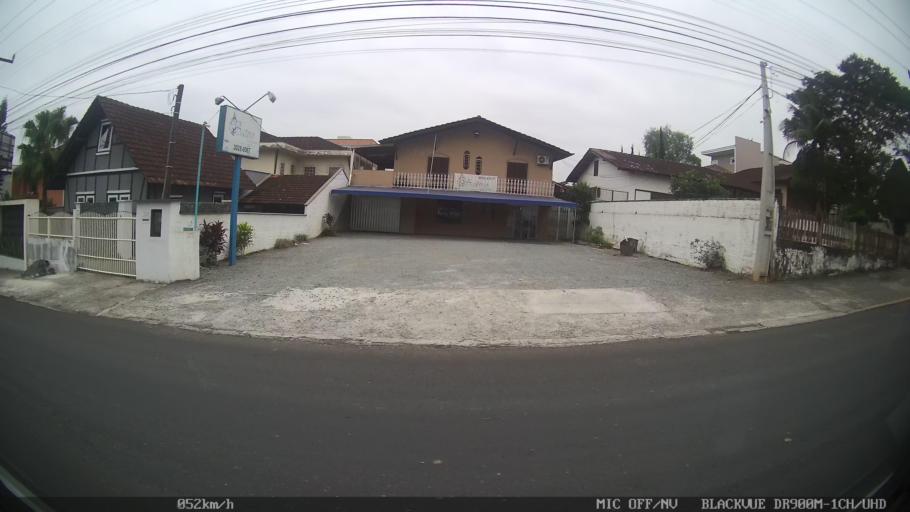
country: BR
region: Santa Catarina
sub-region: Joinville
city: Joinville
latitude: -26.3159
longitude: -48.8597
